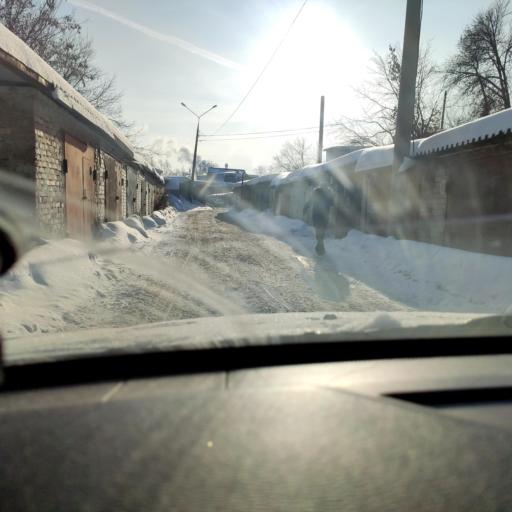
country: RU
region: Samara
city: Volzhskiy
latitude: 53.3883
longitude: 50.1721
